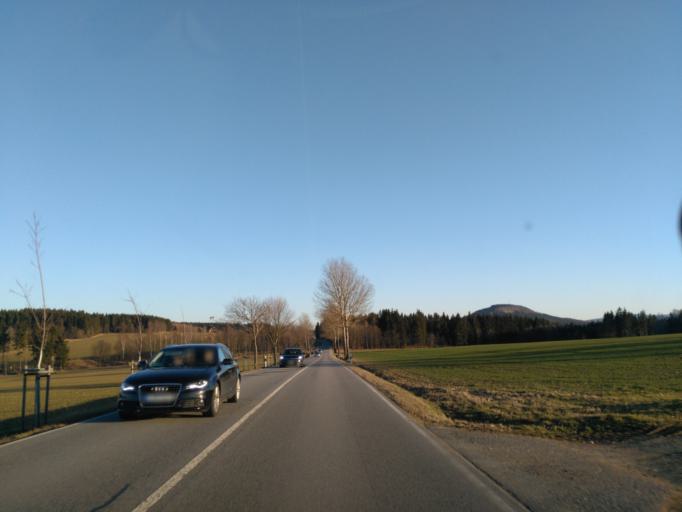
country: DE
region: Saxony
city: Konigswalde
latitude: 50.5406
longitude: 13.0224
